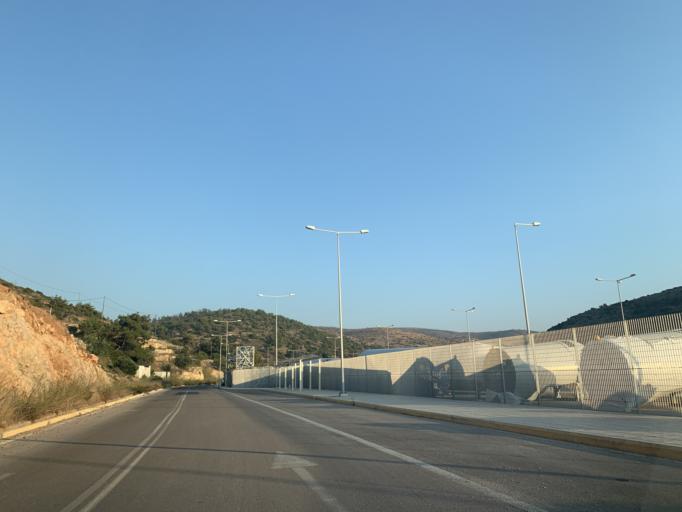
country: GR
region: North Aegean
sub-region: Chios
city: Thymiana
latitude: 38.2915
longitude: 25.9296
